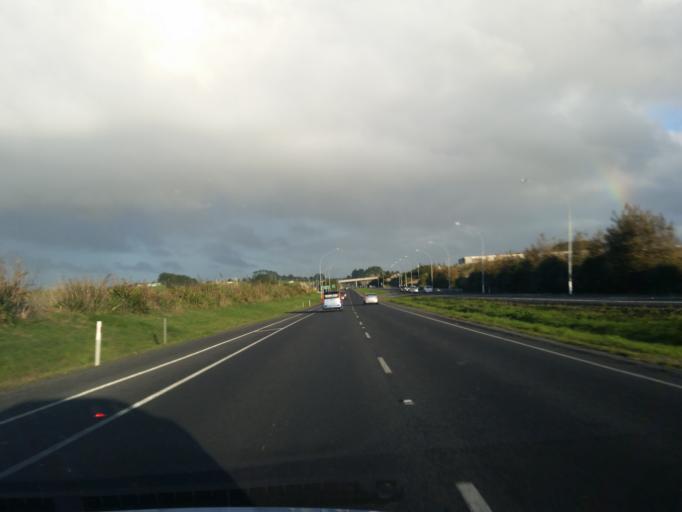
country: NZ
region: Waikato
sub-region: Waikato District
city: Te Kauwhata
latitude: -37.3500
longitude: 175.0788
